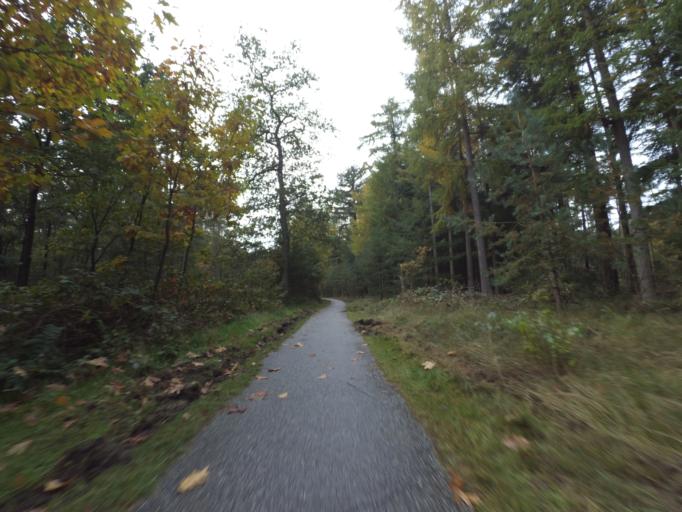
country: NL
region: Gelderland
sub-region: Gemeente Apeldoorn
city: Uddel
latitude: 52.3159
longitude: 5.7447
